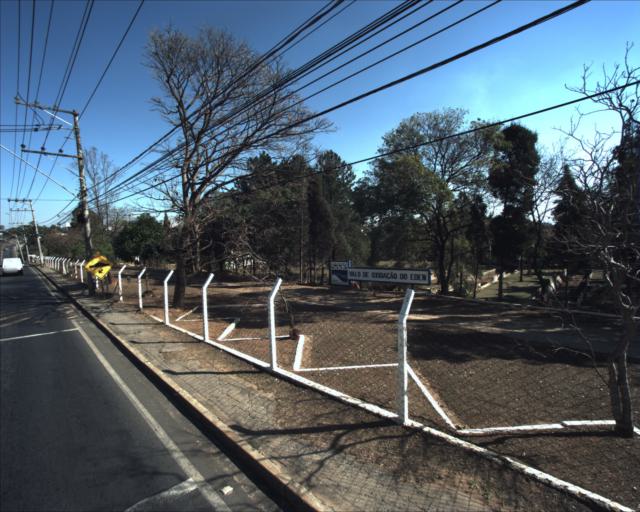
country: BR
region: Sao Paulo
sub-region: Sorocaba
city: Sorocaba
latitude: -23.4495
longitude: -47.4179
